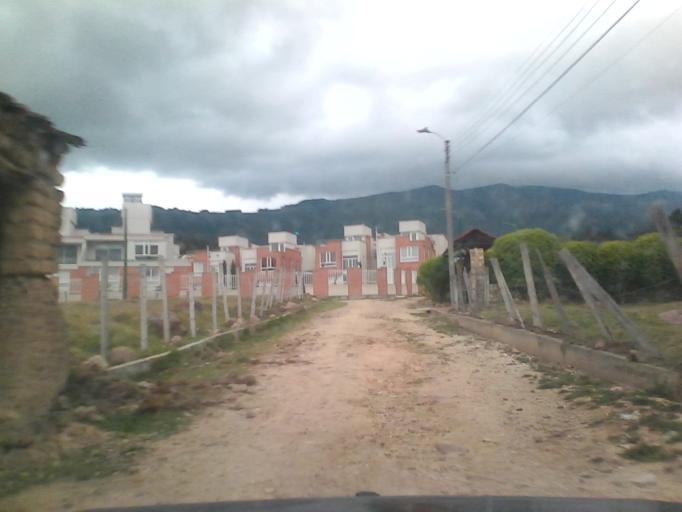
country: CO
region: Boyaca
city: Duitama
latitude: 5.8424
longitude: -73.0340
